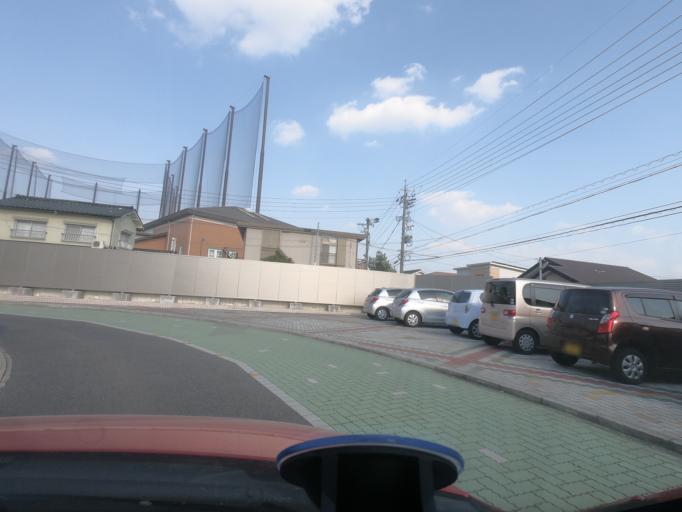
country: JP
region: Aichi
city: Kasugai
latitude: 35.2568
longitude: 136.9834
